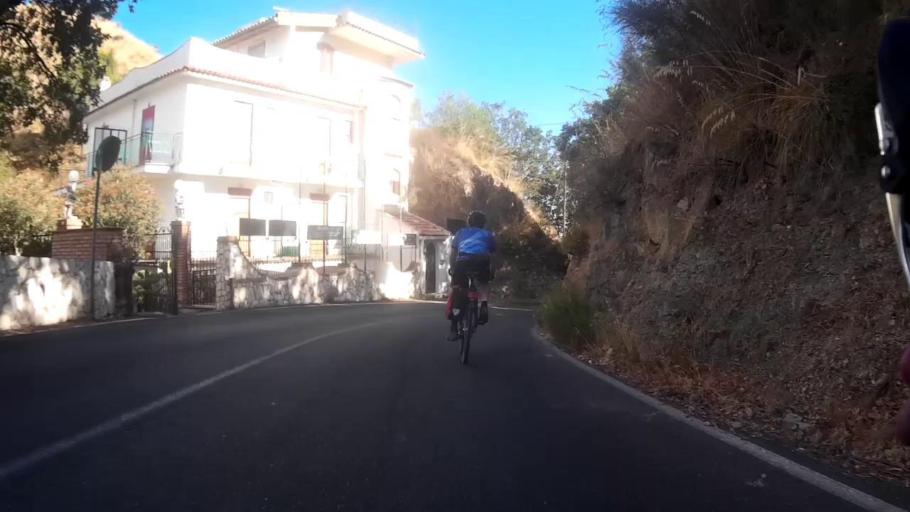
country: IT
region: Sicily
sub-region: Messina
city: Castelmola
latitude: 37.8607
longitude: 15.2800
